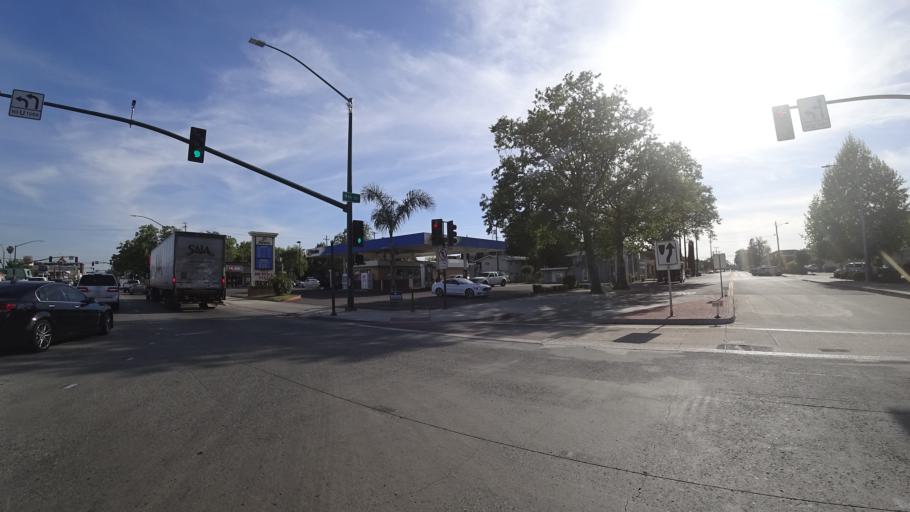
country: US
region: California
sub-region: Yuba County
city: Marysville
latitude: 39.1446
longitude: -121.5912
